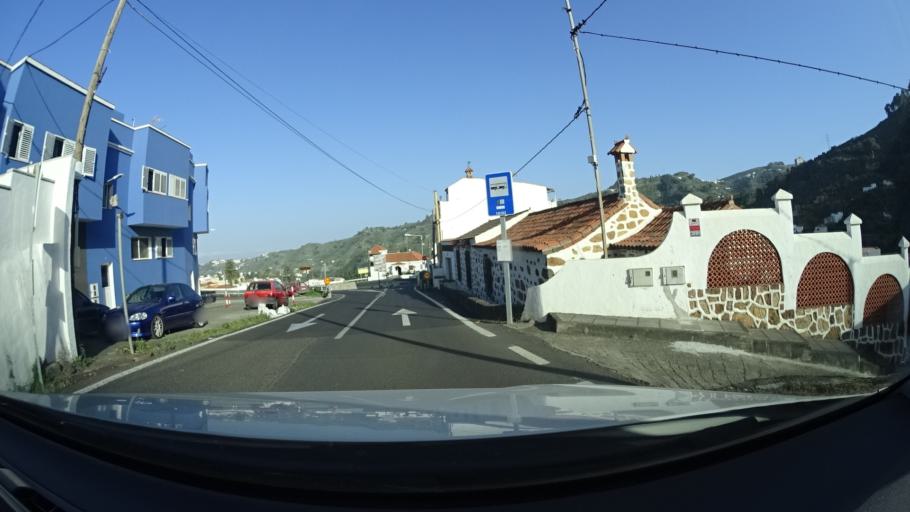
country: ES
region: Canary Islands
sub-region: Provincia de Las Palmas
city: Teror
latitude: 28.0580
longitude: -15.5522
